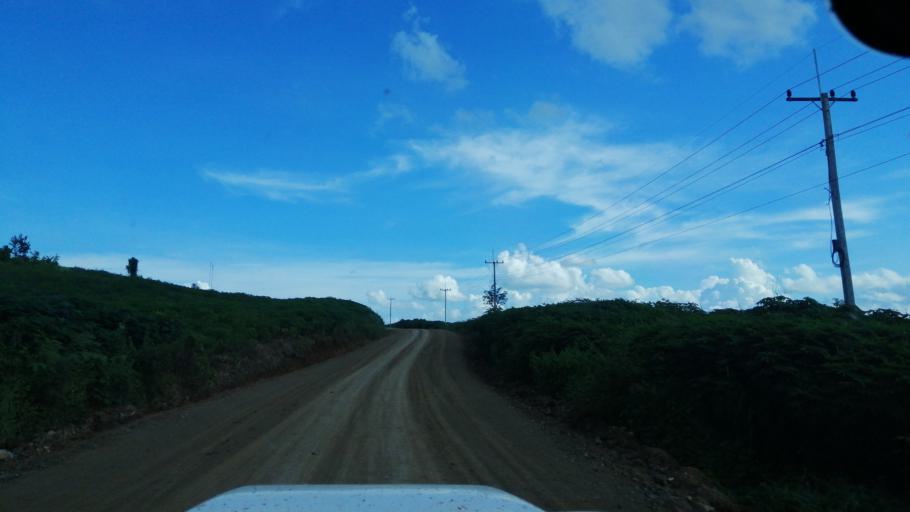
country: LA
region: Xiagnabouli
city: Muang Kenthao
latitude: 17.8620
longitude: 101.2266
